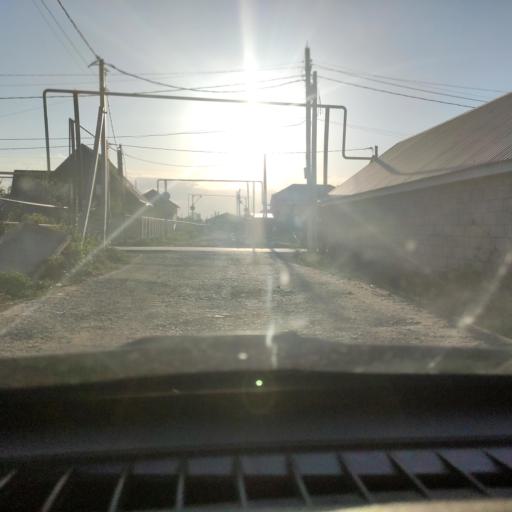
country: RU
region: Samara
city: Tol'yatti
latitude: 53.5636
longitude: 49.4036
